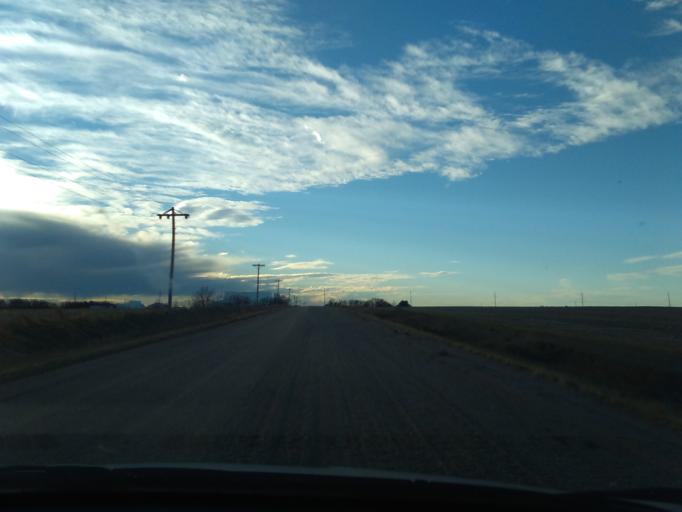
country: US
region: Nebraska
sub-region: Phelps County
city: Holdrege
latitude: 40.4085
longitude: -99.3151
